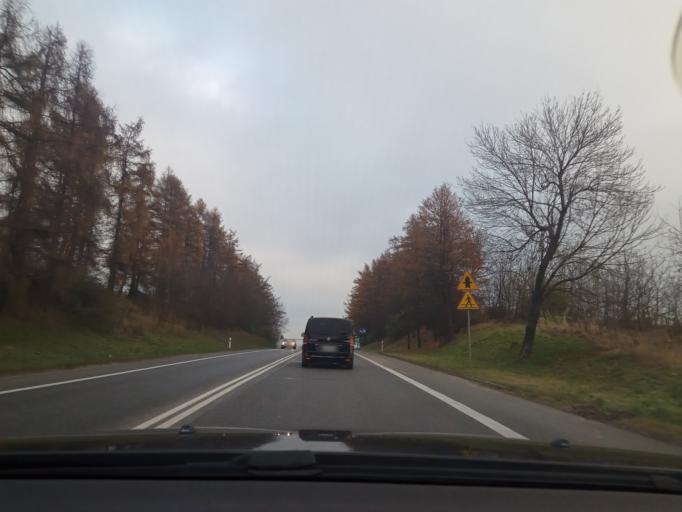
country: PL
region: Lesser Poland Voivodeship
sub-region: Powiat miechowski
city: Miechow
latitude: 50.3479
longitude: 20.0381
